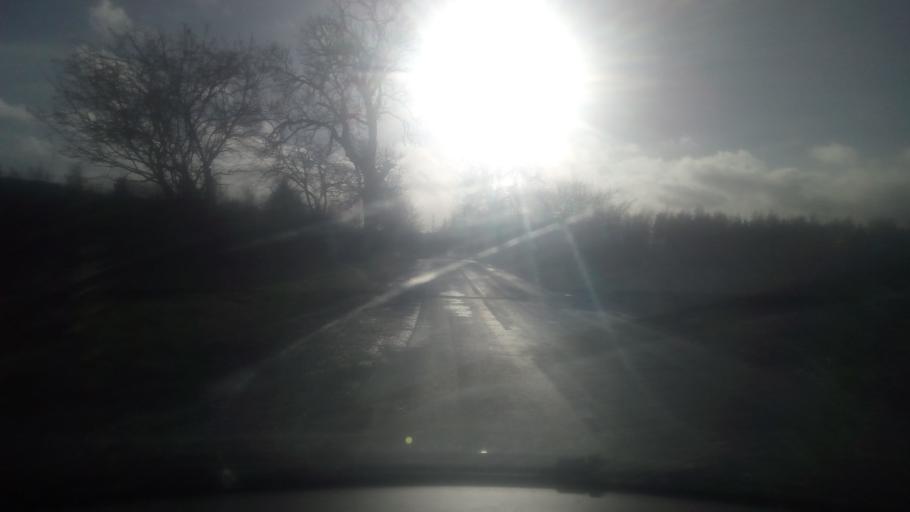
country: GB
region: Scotland
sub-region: The Scottish Borders
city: Coldstream
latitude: 55.7041
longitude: -2.3022
